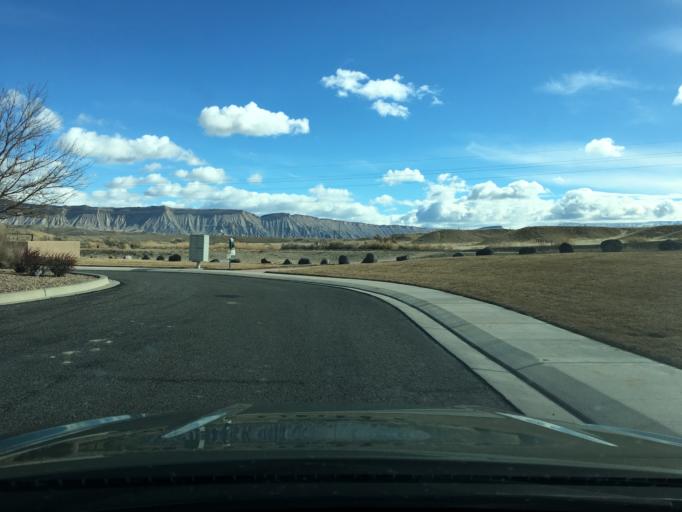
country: US
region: Colorado
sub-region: Mesa County
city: Grand Junction
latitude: 39.1318
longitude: -108.5530
